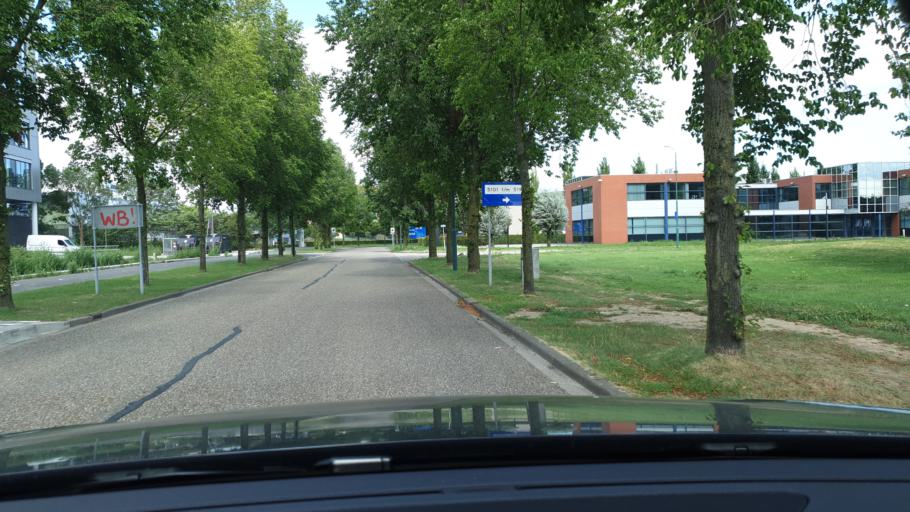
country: NL
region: North Brabant
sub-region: Gemeente Son en Breugel
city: Son
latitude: 51.4981
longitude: 5.4599
